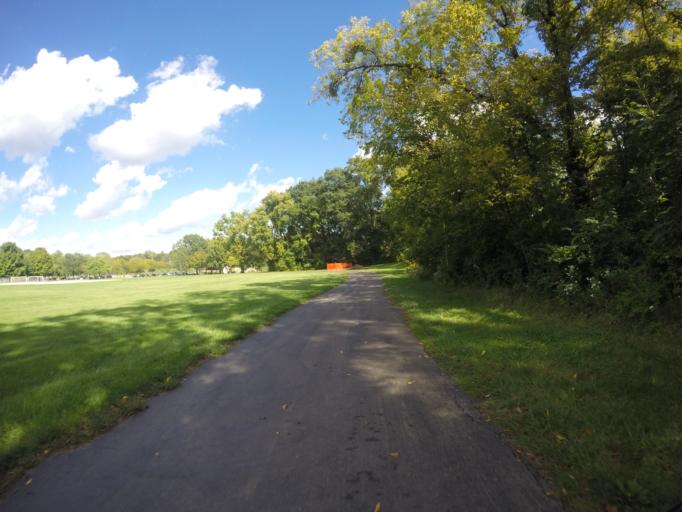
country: US
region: Kansas
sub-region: Johnson County
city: Leawood
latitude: 38.9386
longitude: -94.6427
